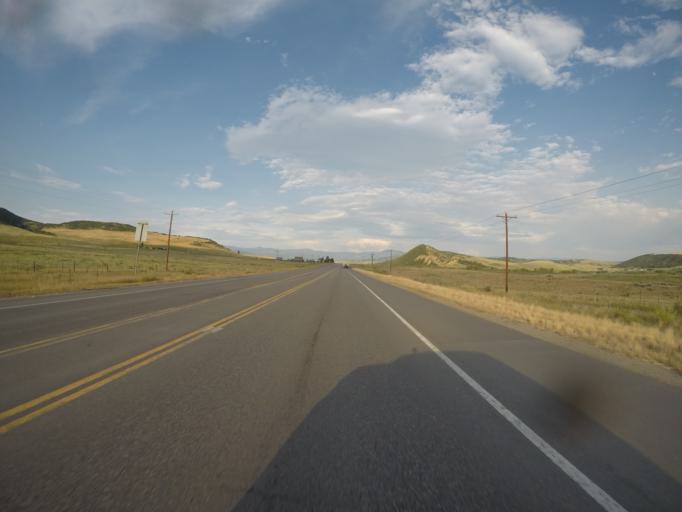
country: US
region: Colorado
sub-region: Routt County
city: Steamboat Springs
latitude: 40.4857
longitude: -107.0139
